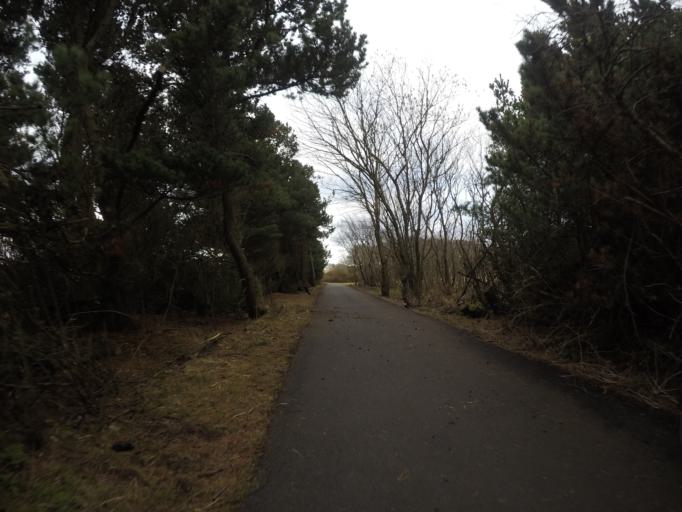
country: GB
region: Scotland
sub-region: North Ayrshire
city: Irvine
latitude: 55.6029
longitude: -4.6810
